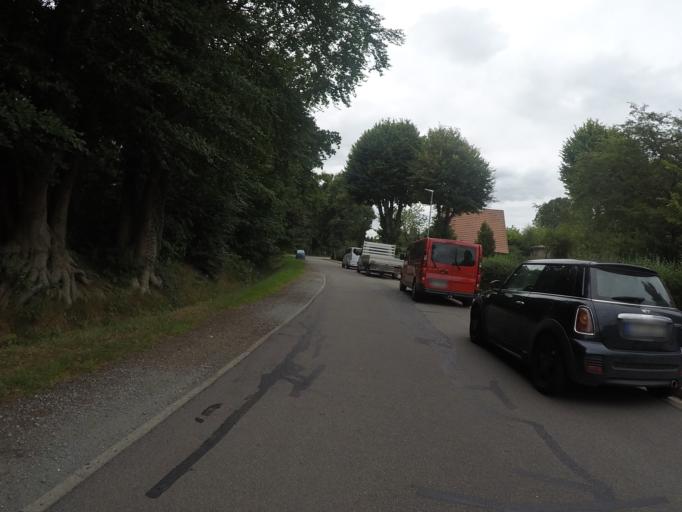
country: DE
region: Lower Saxony
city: Himmelpforten
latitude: 53.6148
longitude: 9.3166
